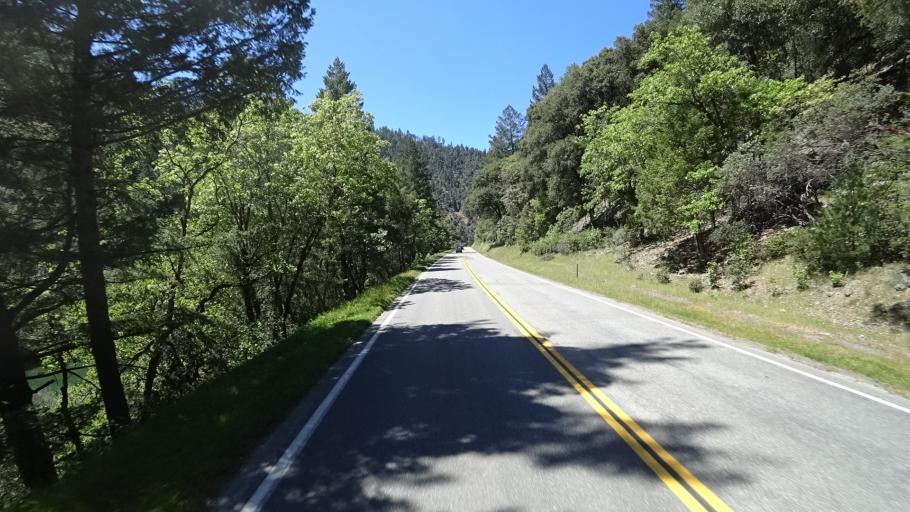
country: US
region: California
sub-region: Trinity County
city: Hayfork
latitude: 40.7511
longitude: -123.2796
